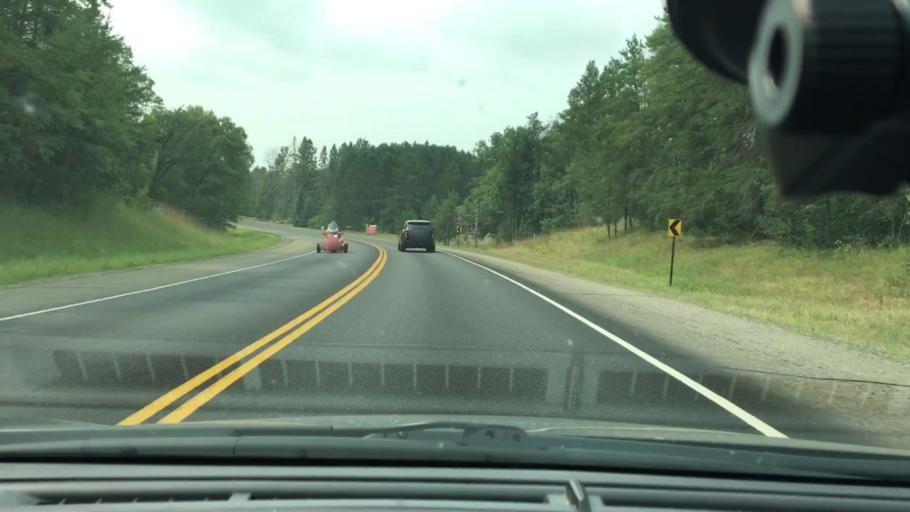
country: US
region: Minnesota
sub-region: Crow Wing County
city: Cross Lake
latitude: 46.6282
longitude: -94.1304
